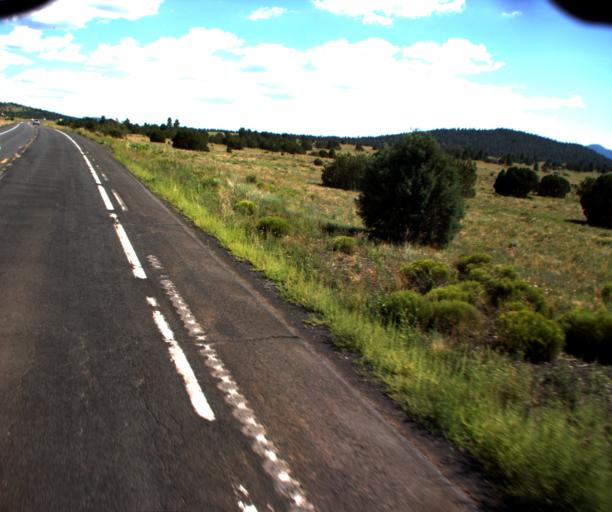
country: US
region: Arizona
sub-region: Coconino County
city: Williams
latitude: 35.3207
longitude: -112.1520
